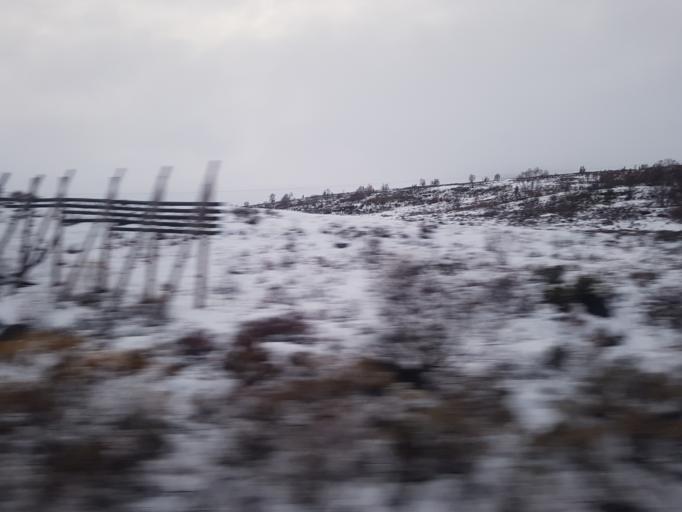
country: NO
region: Sor-Trondelag
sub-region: Oppdal
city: Oppdal
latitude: 62.2786
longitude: 9.5879
